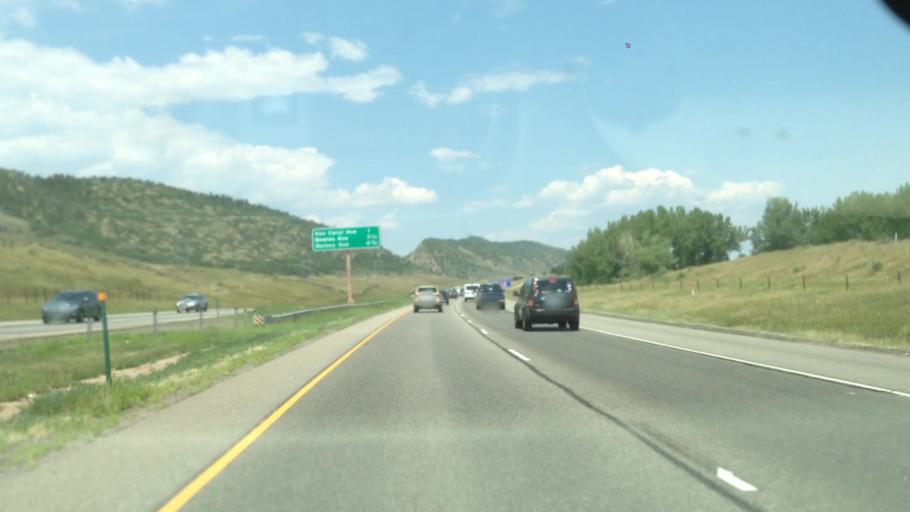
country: US
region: Colorado
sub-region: Jefferson County
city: Ken Caryl
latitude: 39.5648
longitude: -105.1284
